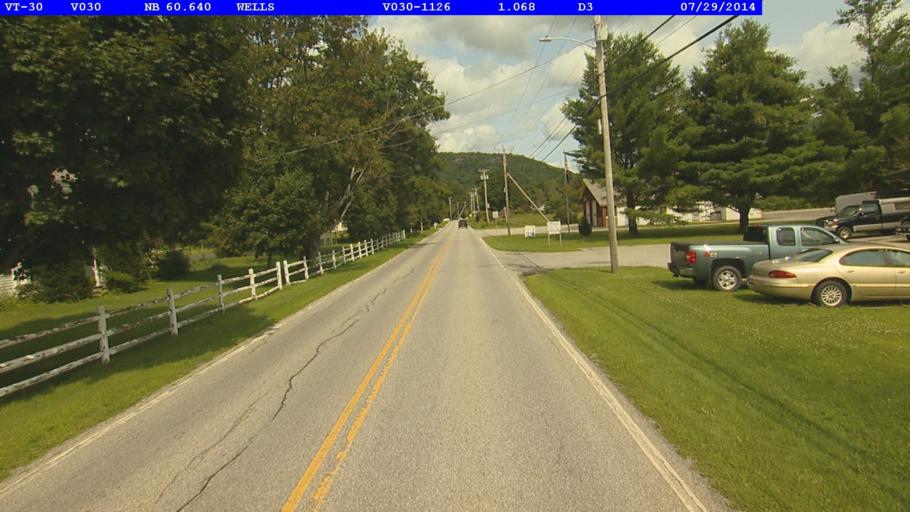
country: US
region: New York
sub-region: Washington County
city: Granville
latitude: 43.4170
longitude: -73.2120
